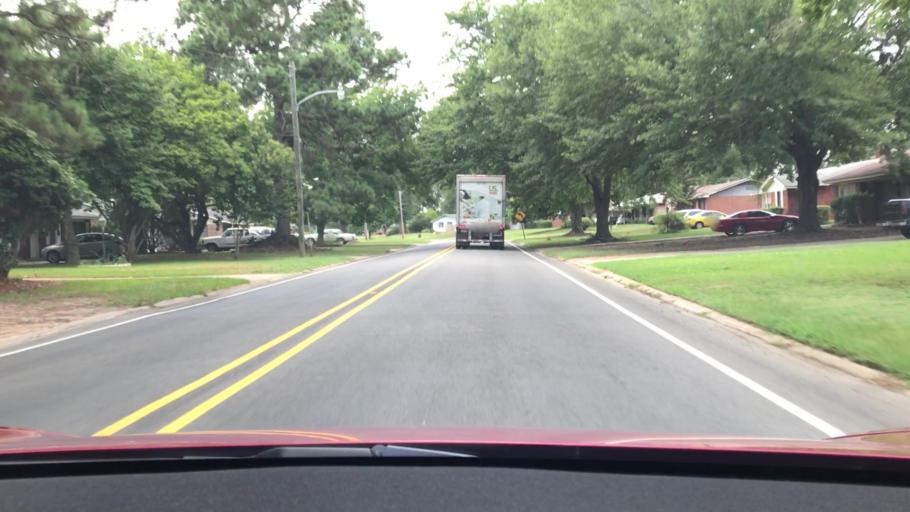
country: US
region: Louisiana
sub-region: De Soto Parish
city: Stonewall
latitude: 32.3955
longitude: -93.8012
